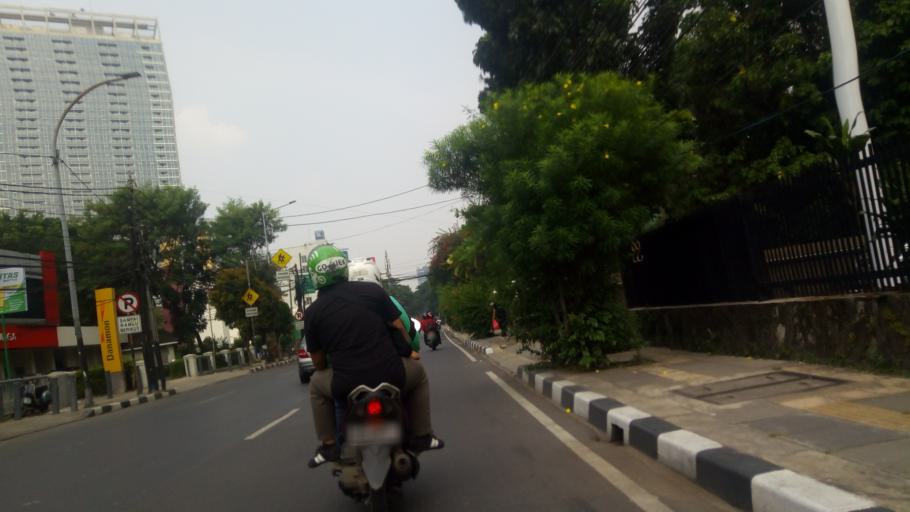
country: ID
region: Jakarta Raya
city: Jakarta
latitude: -6.1897
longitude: 106.8376
